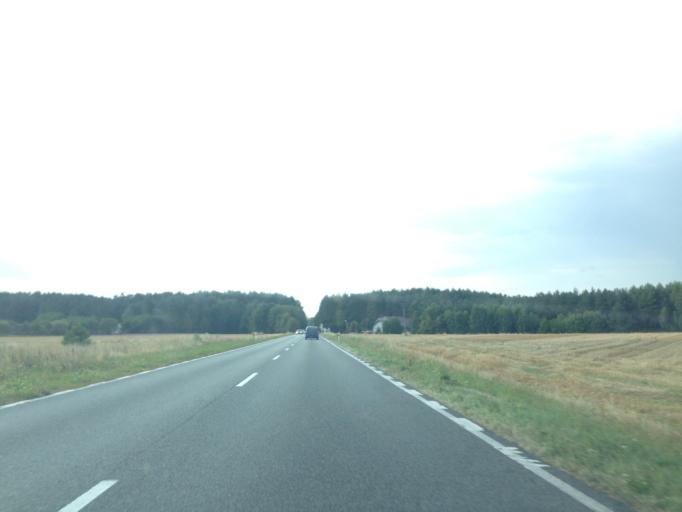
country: PL
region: Kujawsko-Pomorskie
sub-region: Powiat swiecki
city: Swiekatowo
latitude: 53.4802
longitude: 18.1393
